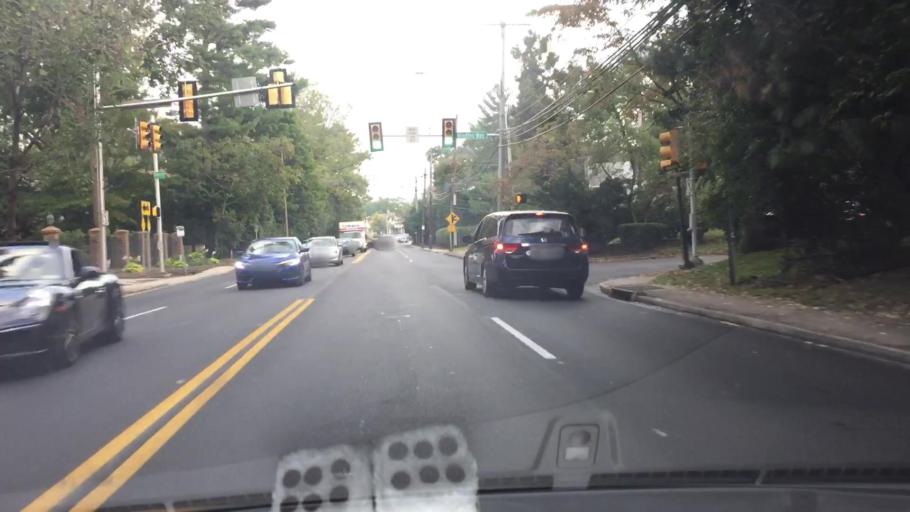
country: US
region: Pennsylvania
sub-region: Montgomery County
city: Bala-Cynwyd
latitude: 40.0068
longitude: -75.2472
